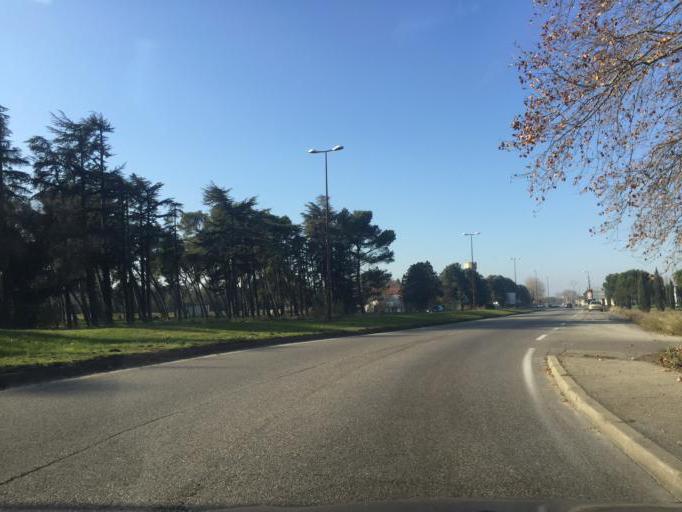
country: FR
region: Provence-Alpes-Cote d'Azur
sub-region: Departement du Vaucluse
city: Montfavet
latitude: 43.9160
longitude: 4.8742
